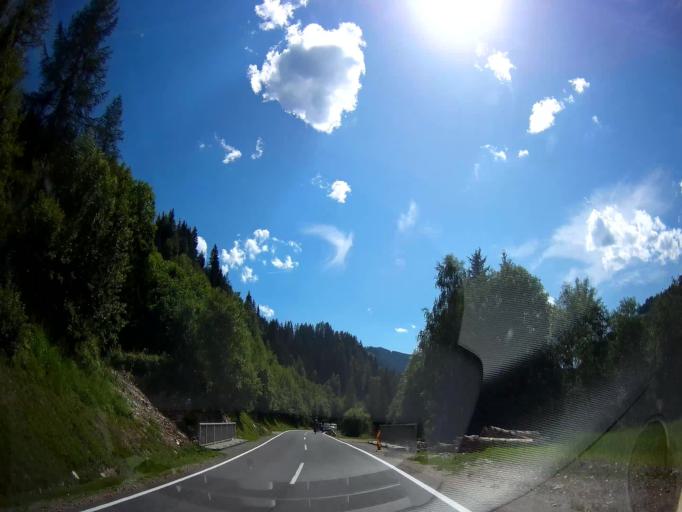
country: AT
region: Styria
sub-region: Politischer Bezirk Murau
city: Stadl an der Mur
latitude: 47.0763
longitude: 13.9235
